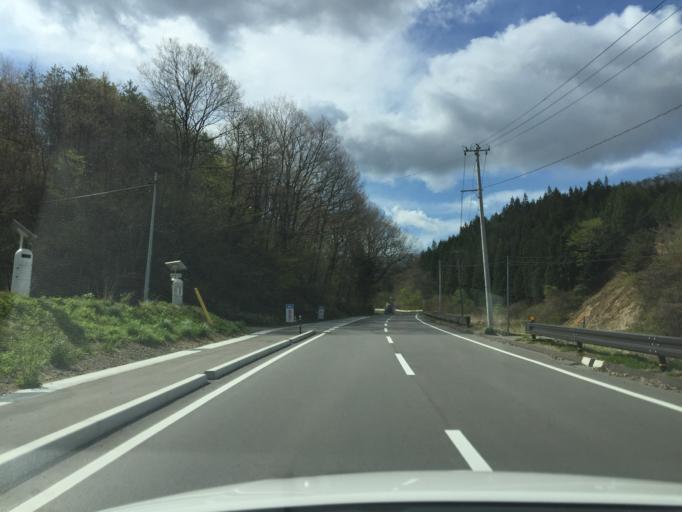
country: JP
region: Fukushima
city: Funehikimachi-funehiki
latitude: 37.6221
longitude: 140.6455
